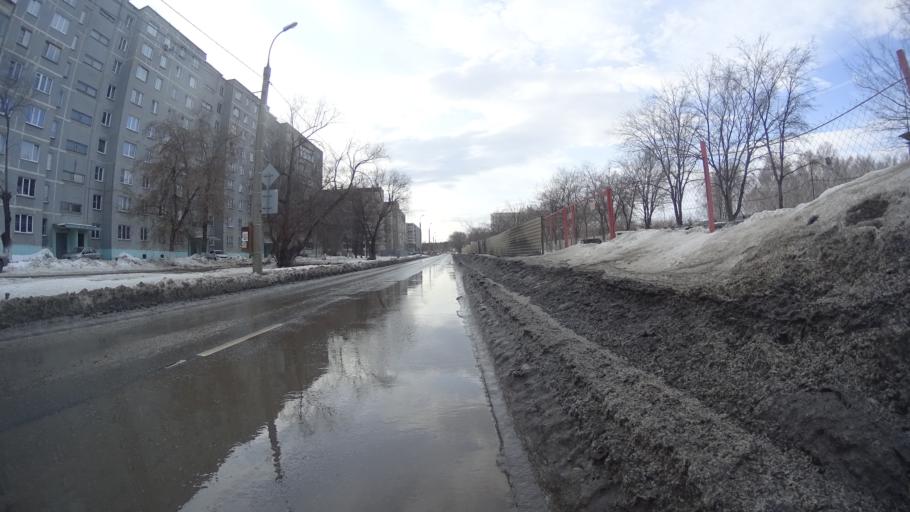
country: RU
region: Chelyabinsk
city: Roshchino
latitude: 55.1988
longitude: 61.3116
